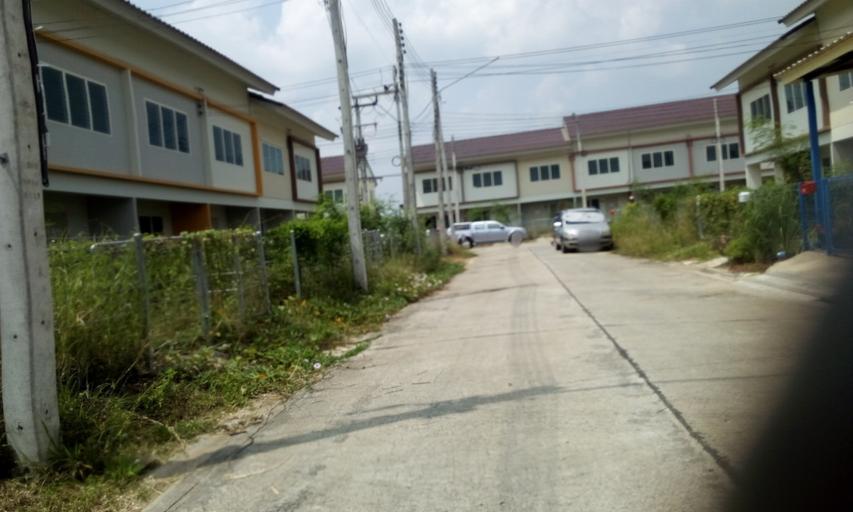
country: TH
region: Pathum Thani
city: Nong Suea
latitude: 14.0637
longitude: 100.8227
